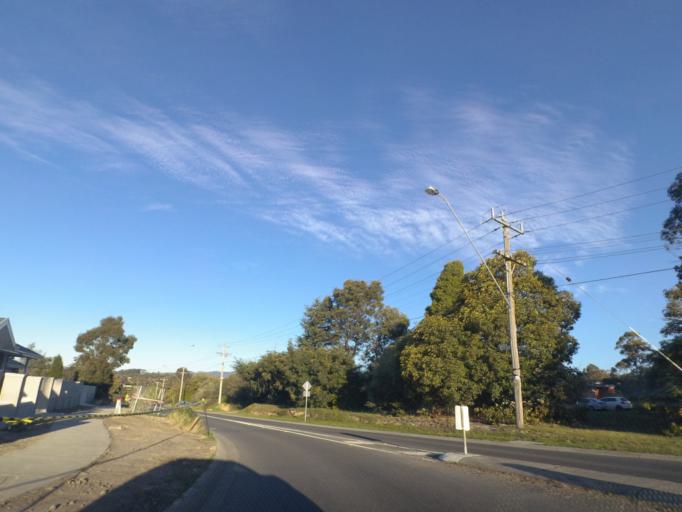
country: AU
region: Victoria
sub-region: Manningham
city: Park Orchards
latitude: -37.7837
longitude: 145.2276
